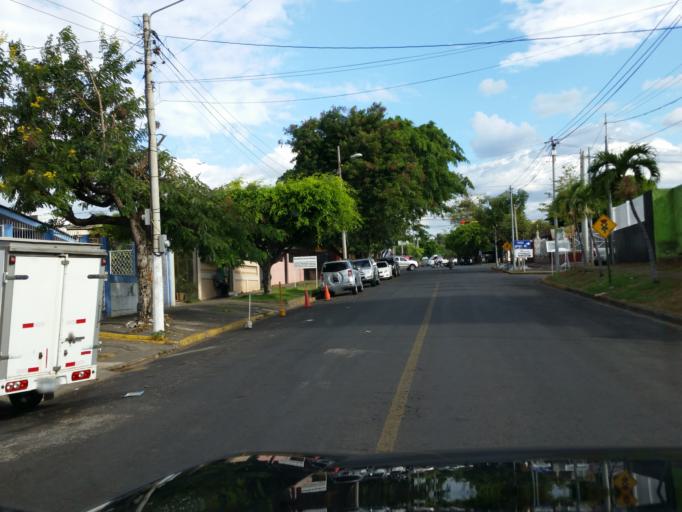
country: NI
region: Managua
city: Managua
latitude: 12.1261
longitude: -86.2581
